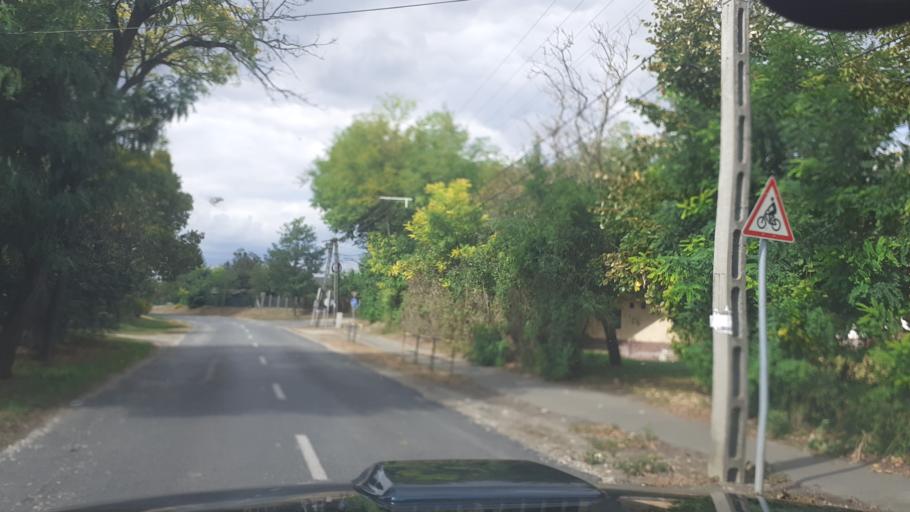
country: HU
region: Bacs-Kiskun
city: Solt
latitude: 46.8125
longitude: 18.9825
